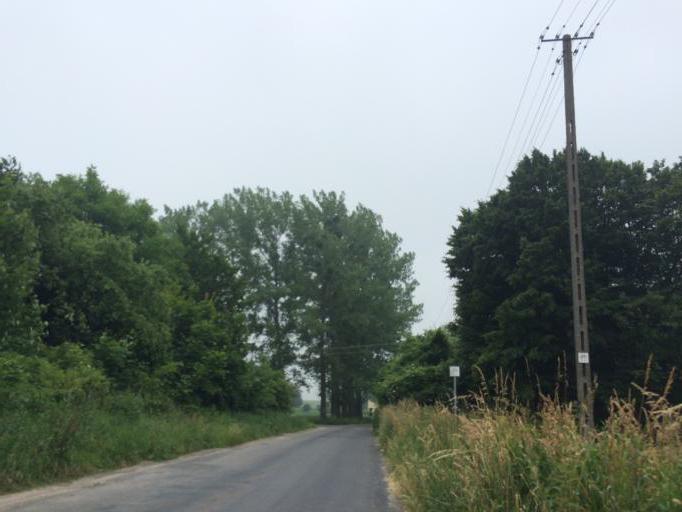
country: PL
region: Lublin Voivodeship
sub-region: Powiat pulawski
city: Markuszow
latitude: 51.3631
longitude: 22.2541
